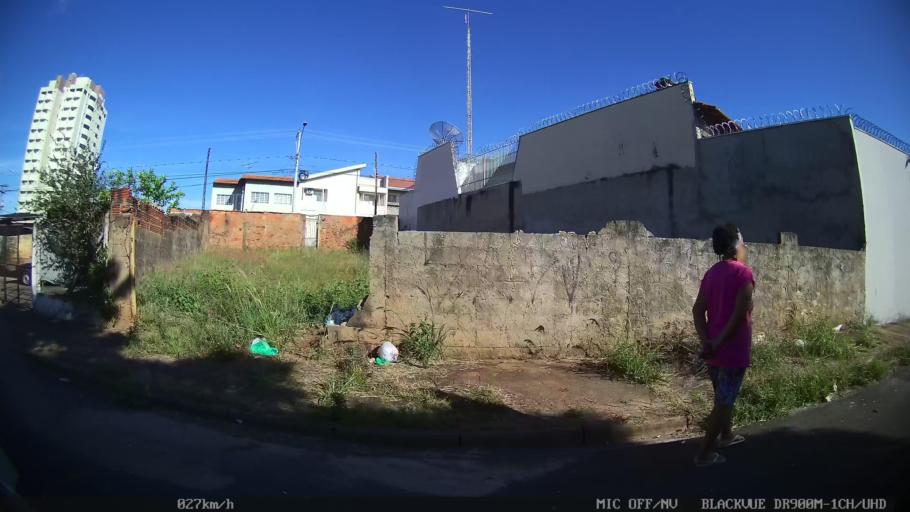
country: BR
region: Sao Paulo
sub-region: Franca
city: Franca
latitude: -20.5480
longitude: -47.4094
